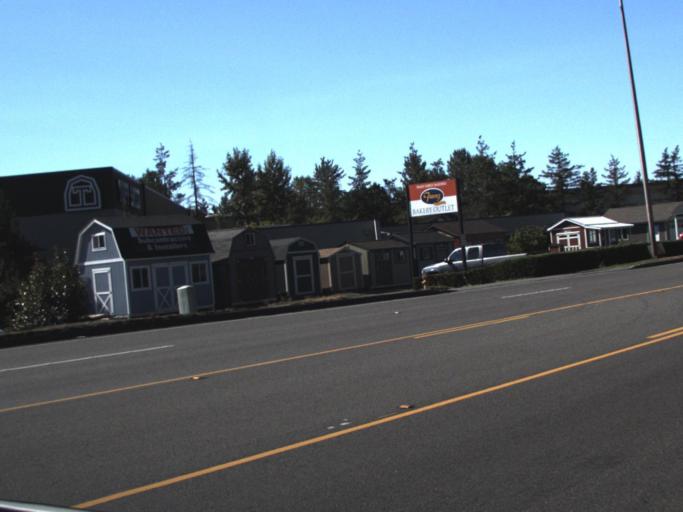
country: US
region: Washington
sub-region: King County
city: Tukwila
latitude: 47.4466
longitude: -122.2440
